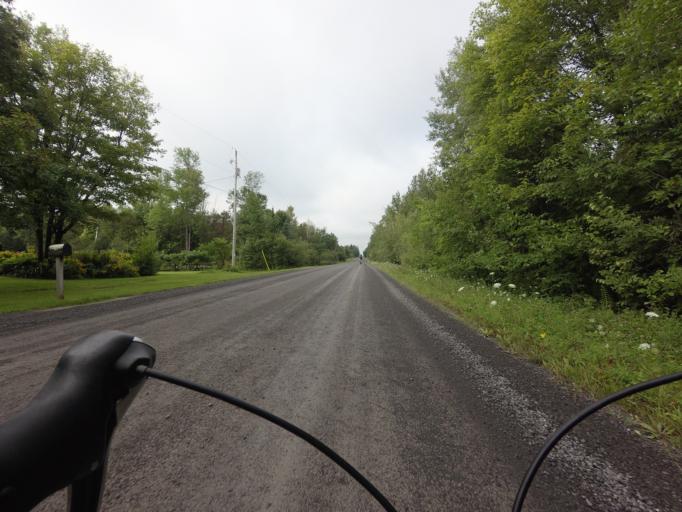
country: CA
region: Ontario
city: Bells Corners
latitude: 45.0400
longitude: -75.7420
